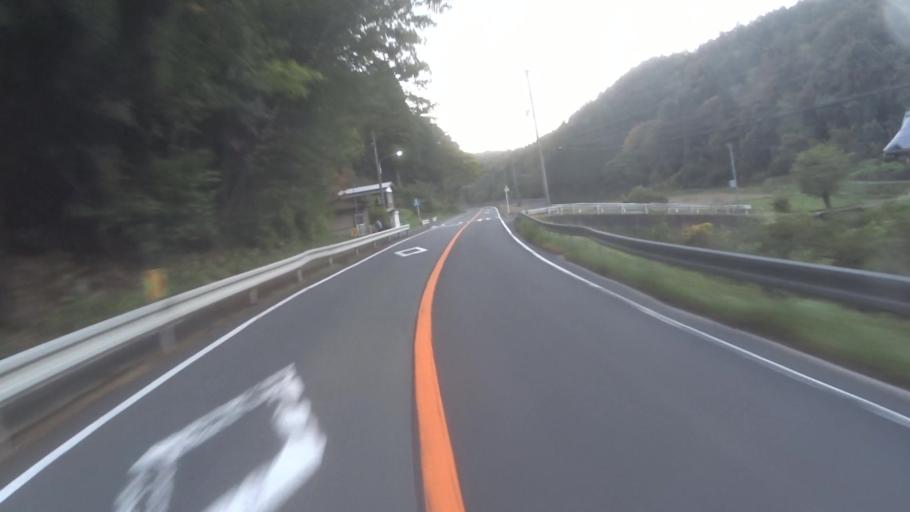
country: JP
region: Kyoto
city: Ayabe
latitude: 35.2278
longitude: 135.3362
